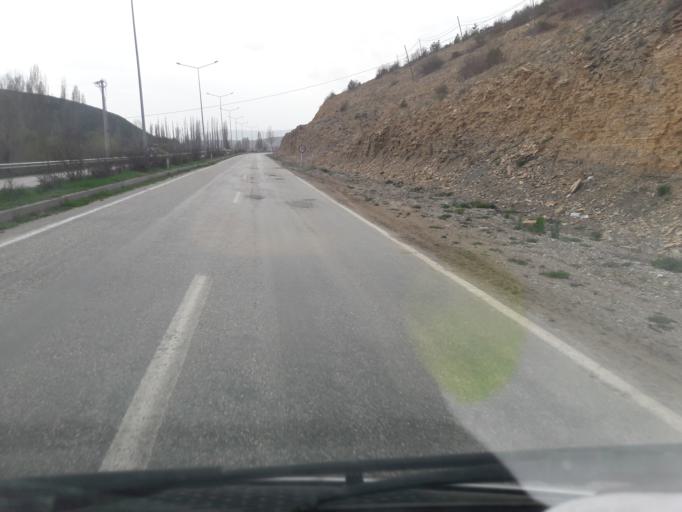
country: TR
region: Gumushane
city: Siran
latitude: 40.1765
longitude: 39.1325
